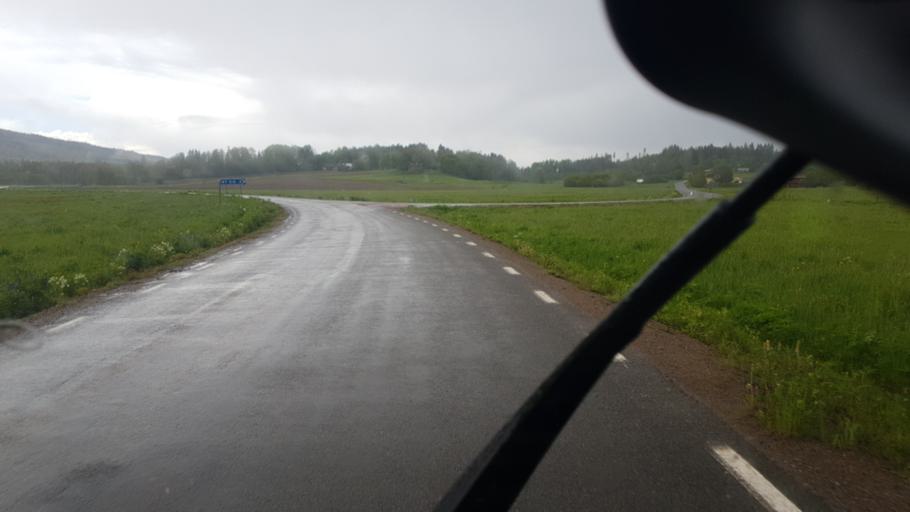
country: SE
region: Vaermland
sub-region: Eda Kommun
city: Amotfors
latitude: 59.7088
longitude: 12.4498
